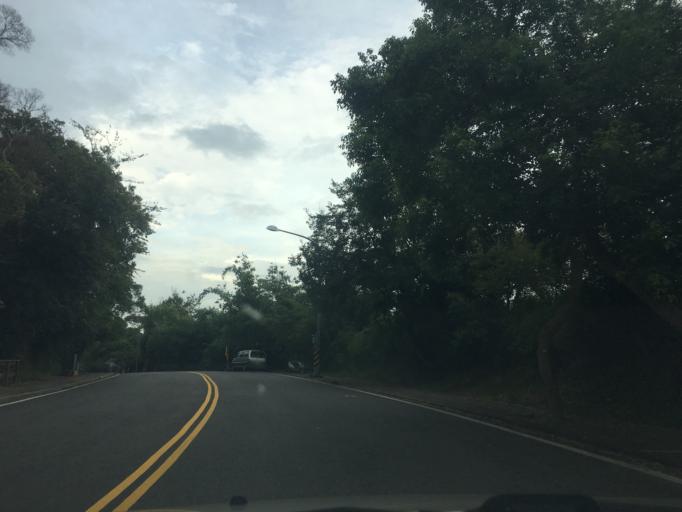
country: TW
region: Taiwan
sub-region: Changhua
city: Chang-hua
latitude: 24.0630
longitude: 120.5710
